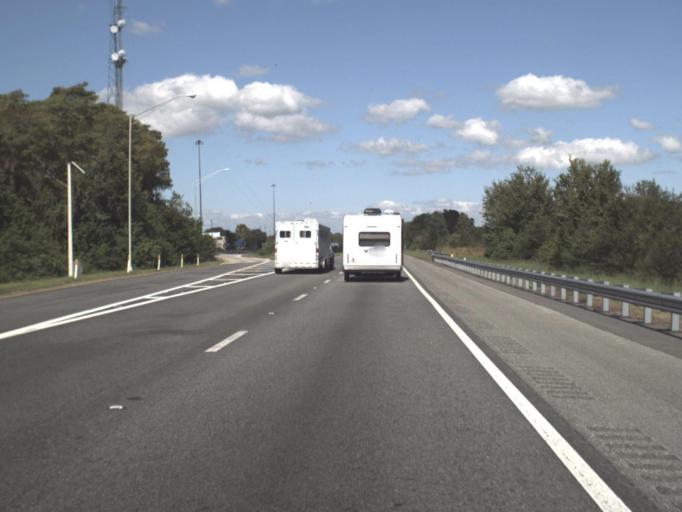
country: US
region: Florida
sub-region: Osceola County
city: Saint Cloud
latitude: 28.0910
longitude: -81.2701
